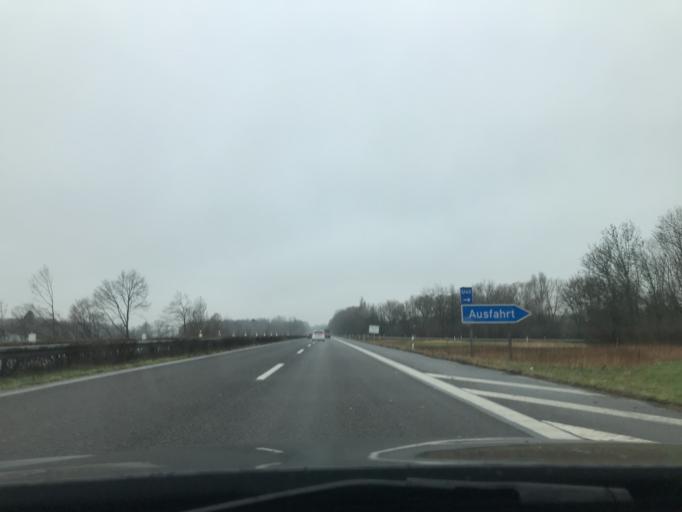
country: DE
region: North Rhine-Westphalia
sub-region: Regierungsbezirk Dusseldorf
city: Sonsbeck
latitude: 51.6042
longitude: 6.3513
